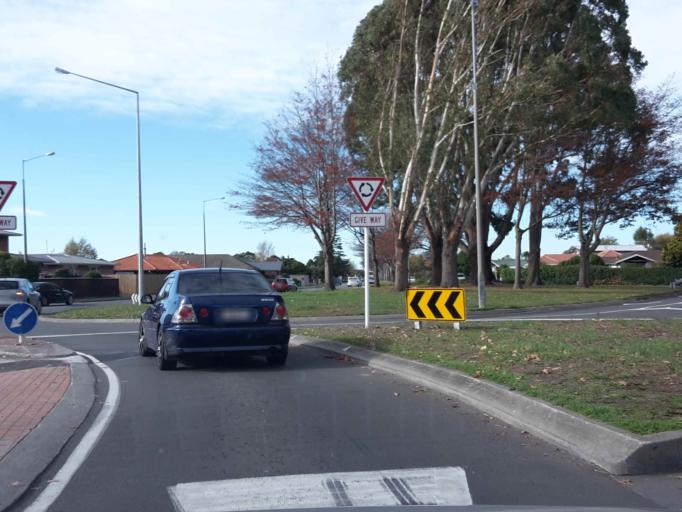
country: NZ
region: Canterbury
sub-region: Christchurch City
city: Christchurch
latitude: -43.4879
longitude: 172.5879
